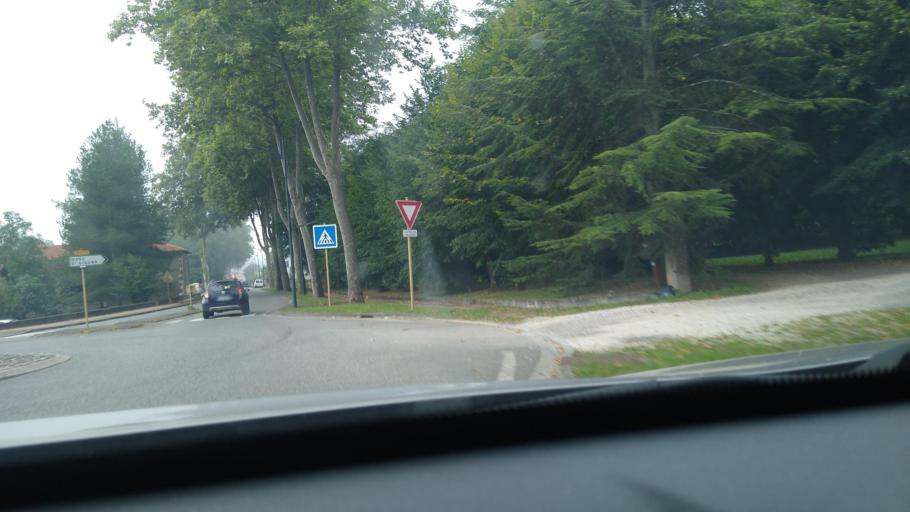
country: FR
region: Midi-Pyrenees
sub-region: Departement de la Haute-Garonne
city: Salies-du-Salat
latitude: 43.0887
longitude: 0.9508
